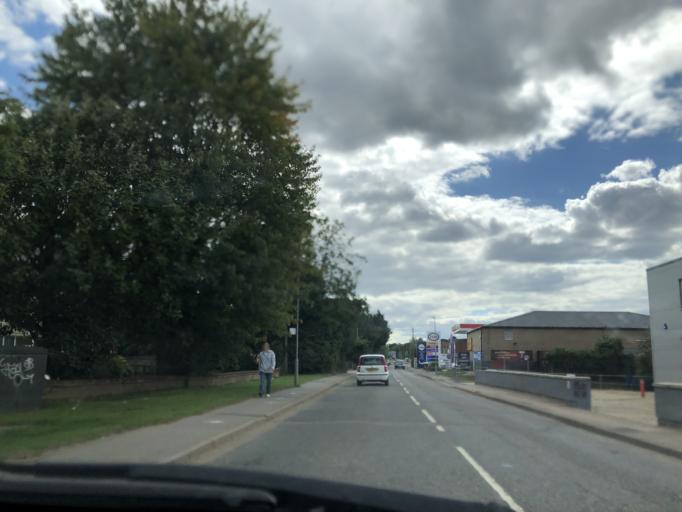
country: GB
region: England
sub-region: Kent
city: Edenbridge
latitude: 51.2069
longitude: 0.0616
